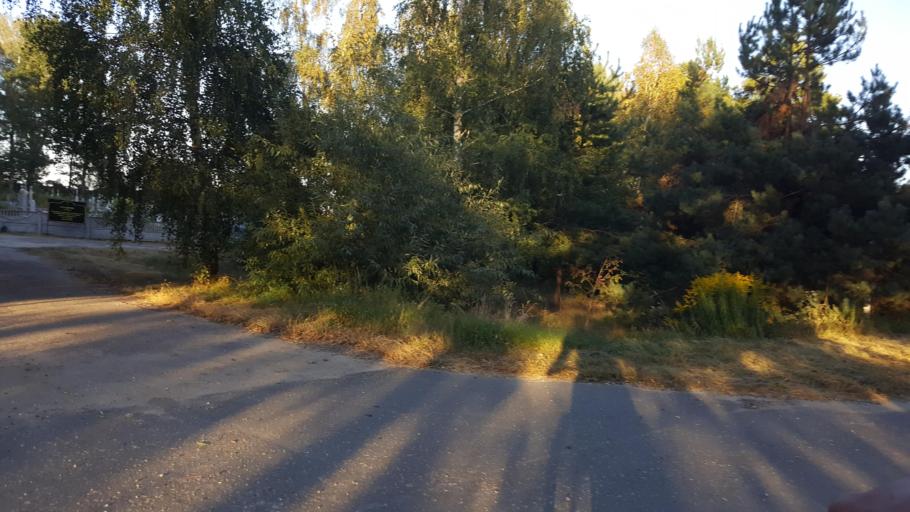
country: BY
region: Brest
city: Vysokaye
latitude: 52.3041
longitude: 23.4667
